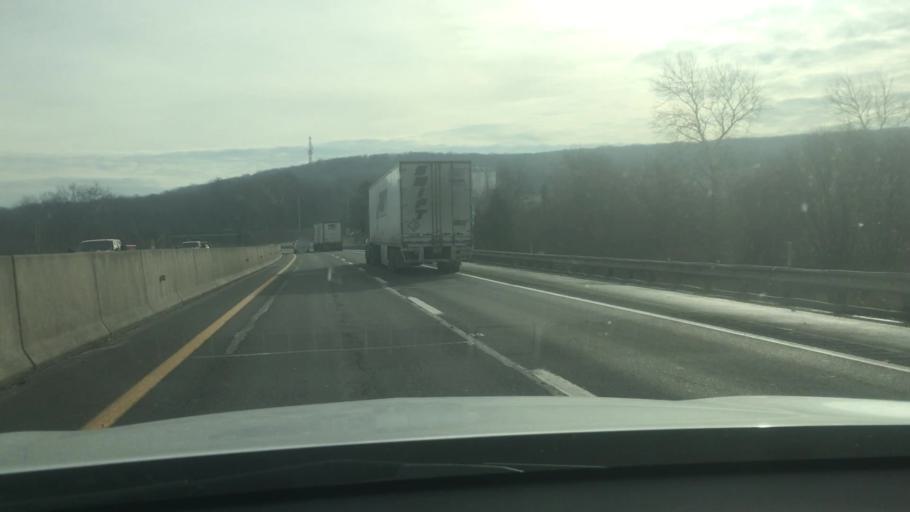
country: US
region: Pennsylvania
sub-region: Chester County
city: Elverson
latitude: 40.1496
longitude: -75.8577
